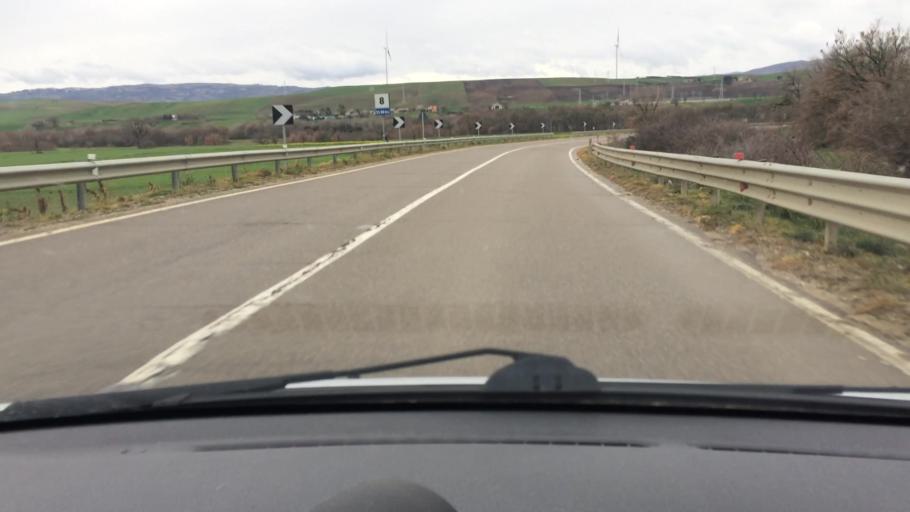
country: IT
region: Basilicate
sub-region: Provincia di Potenza
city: San Chirico Nuovo
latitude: 40.7726
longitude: 16.1204
